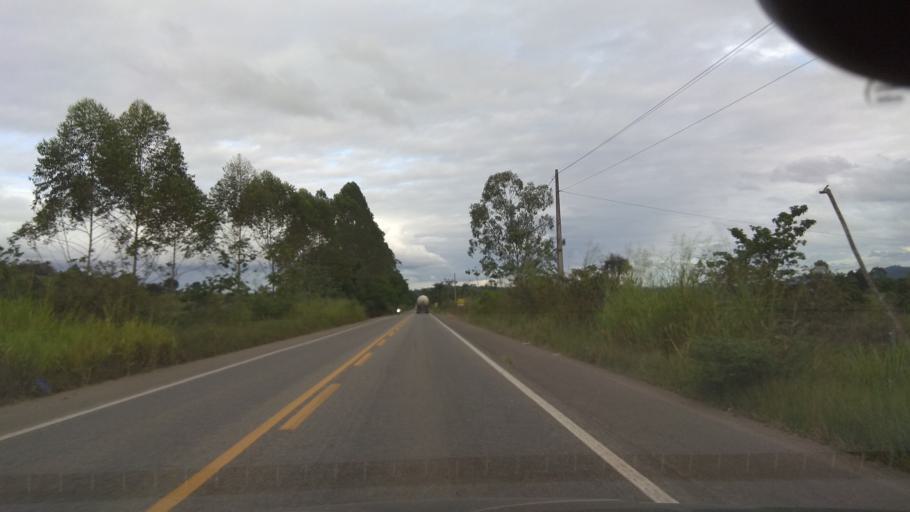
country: BR
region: Bahia
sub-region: Ipiau
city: Ipiau
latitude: -14.1610
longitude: -39.6918
